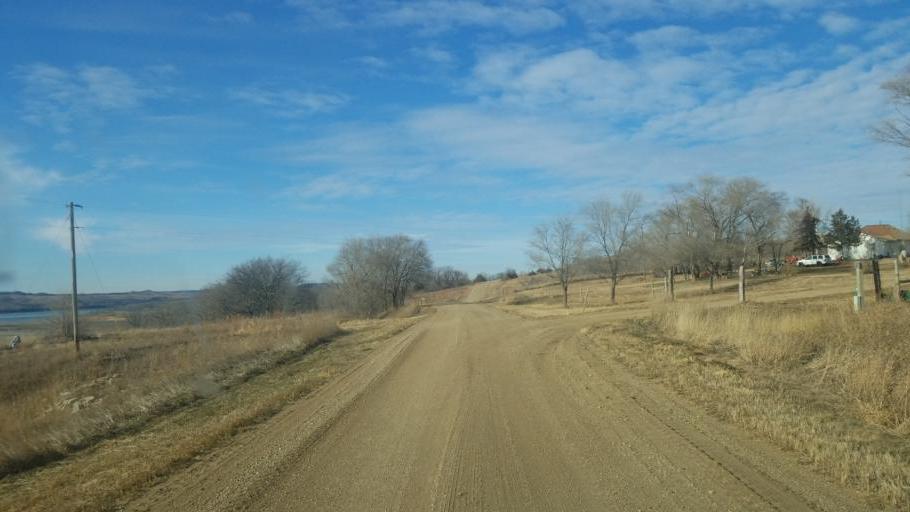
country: US
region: South Dakota
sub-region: Charles Mix County
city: Wagner
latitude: 42.9296
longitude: -98.4072
